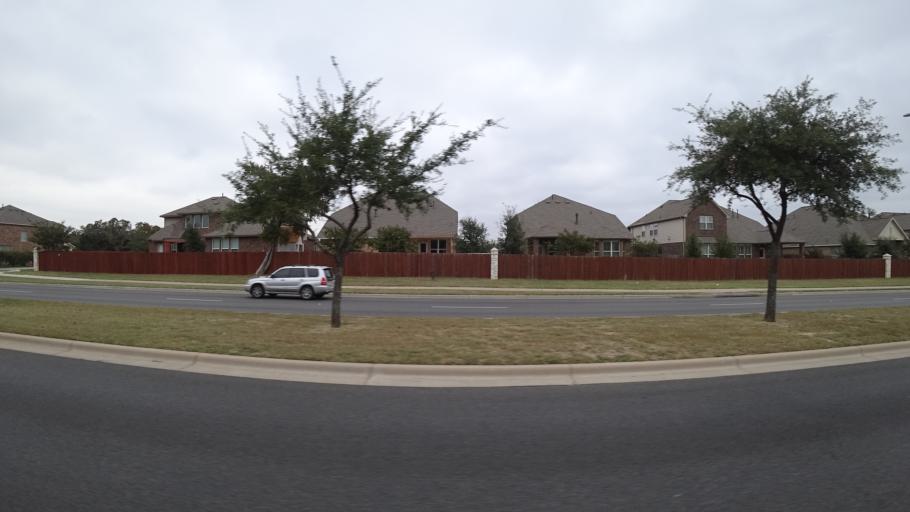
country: US
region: Texas
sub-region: Williamson County
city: Cedar Park
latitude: 30.4964
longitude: -97.8426
